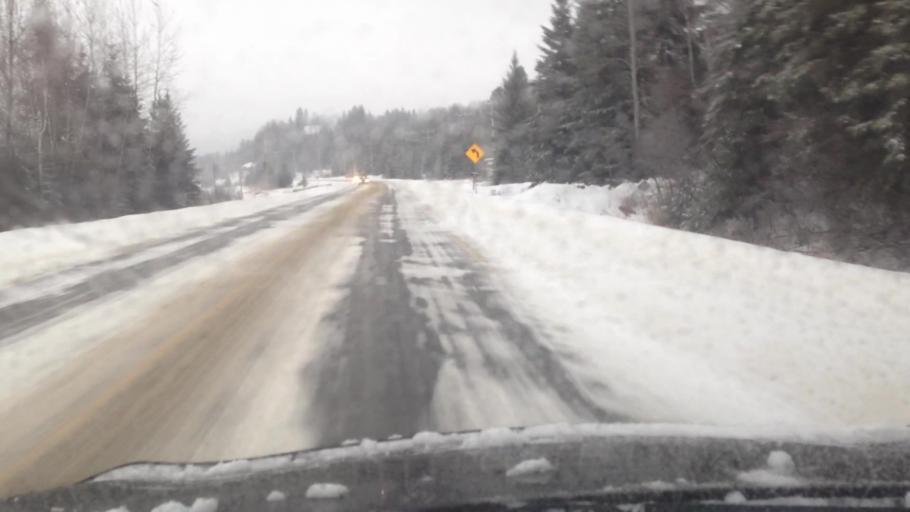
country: CA
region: Quebec
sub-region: Laurentides
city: Mont-Tremblant
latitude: 46.0780
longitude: -74.6161
